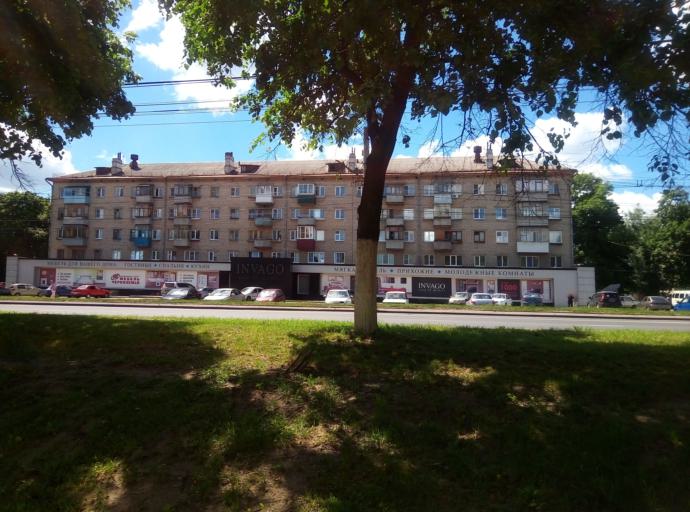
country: RU
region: Kursk
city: Kursk
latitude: 51.7697
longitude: 36.1817
